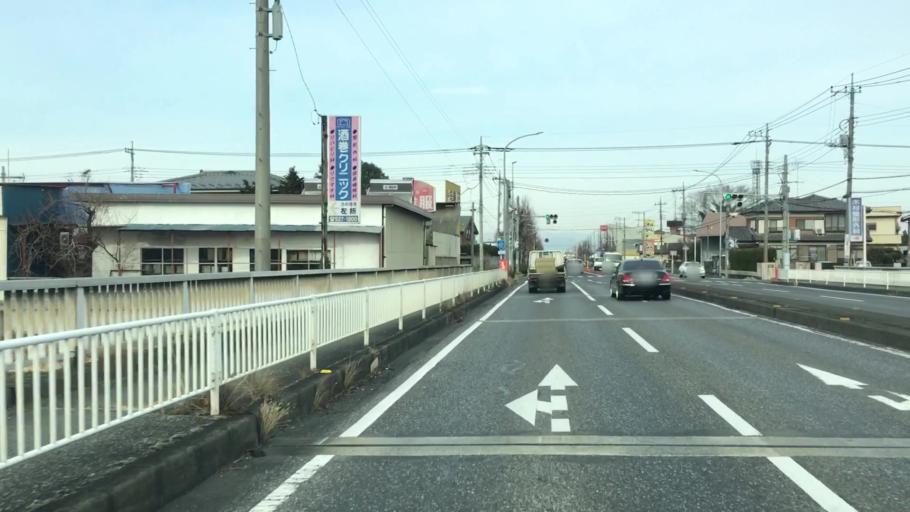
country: JP
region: Saitama
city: Kumagaya
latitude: 36.1637
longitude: 139.3707
